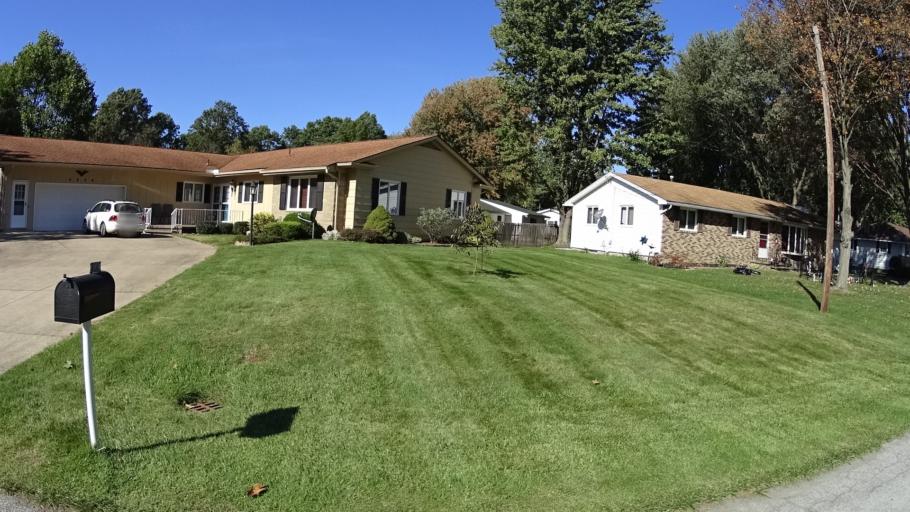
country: US
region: Ohio
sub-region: Lorain County
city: Lorain
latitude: 41.4192
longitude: -82.1769
